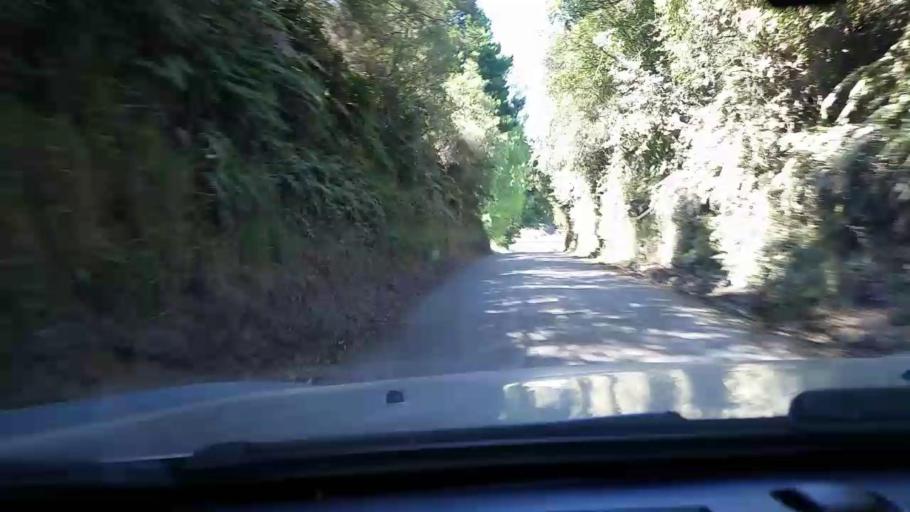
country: NZ
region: Bay of Plenty
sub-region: Rotorua District
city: Rotorua
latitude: -38.3805
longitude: 176.2018
